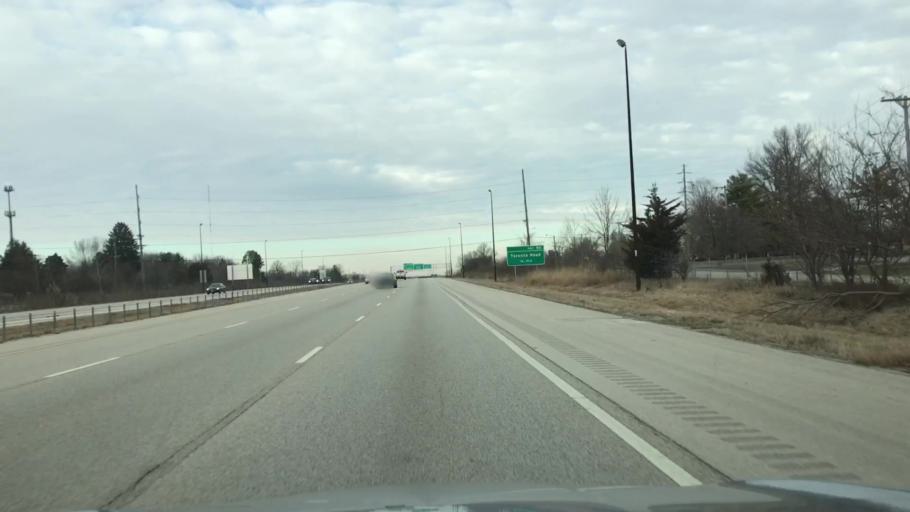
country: US
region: Illinois
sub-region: Sangamon County
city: Southern View
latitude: 39.7052
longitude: -89.6435
